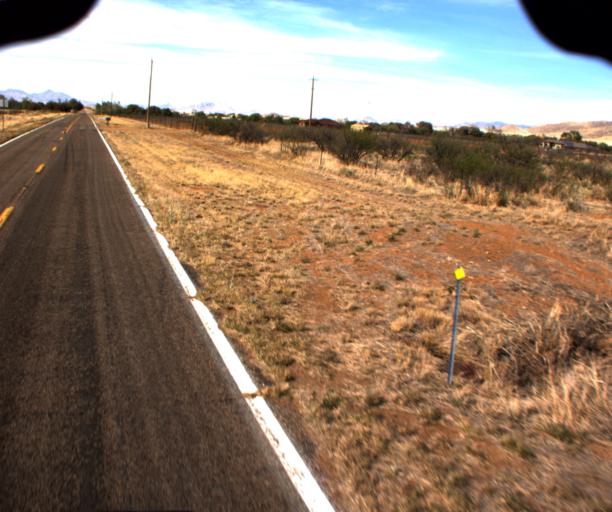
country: US
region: Arizona
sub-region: Cochise County
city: Willcox
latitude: 31.8825
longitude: -109.4913
